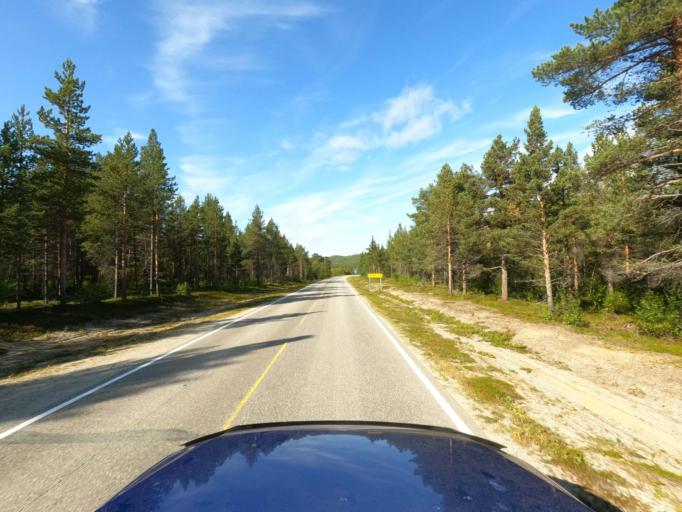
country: NO
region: Finnmark Fylke
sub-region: Porsanger
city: Lakselv
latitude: 69.8239
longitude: 25.1507
